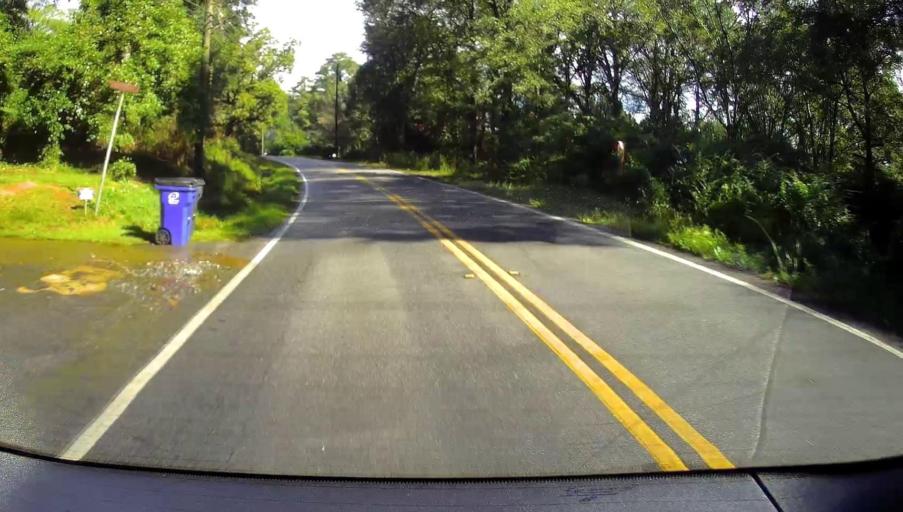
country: US
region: Georgia
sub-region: Bibb County
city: Macon
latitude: 32.8850
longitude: -83.7175
